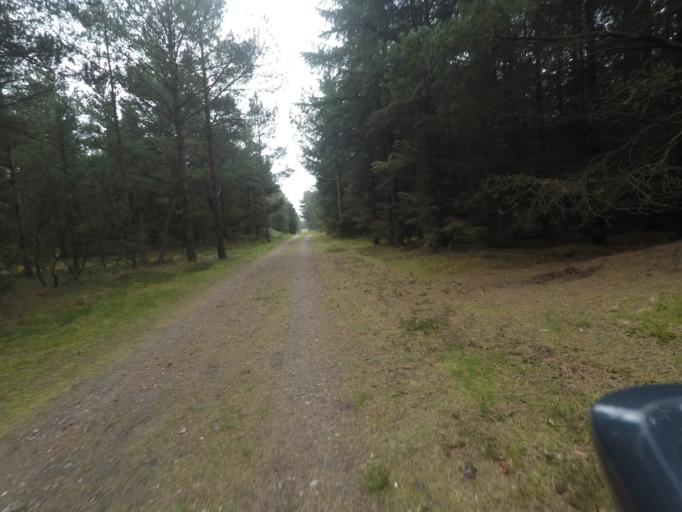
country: DE
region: Schleswig-Holstein
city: List
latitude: 55.1009
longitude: 8.5243
